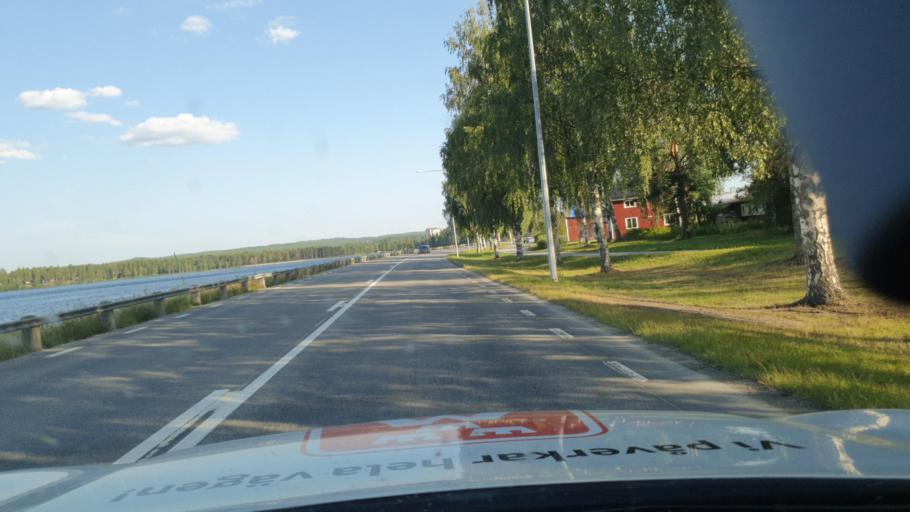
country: SE
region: Vaesterbotten
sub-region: Lycksele Kommun
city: Lycksele
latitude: 64.6004
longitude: 18.6795
